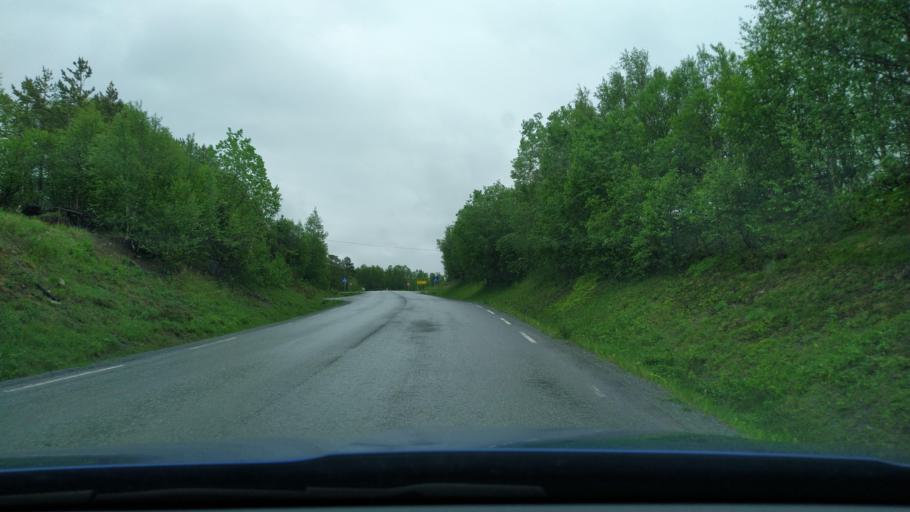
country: NO
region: Troms
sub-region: Dyroy
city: Brostadbotn
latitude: 69.0824
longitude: 17.6933
